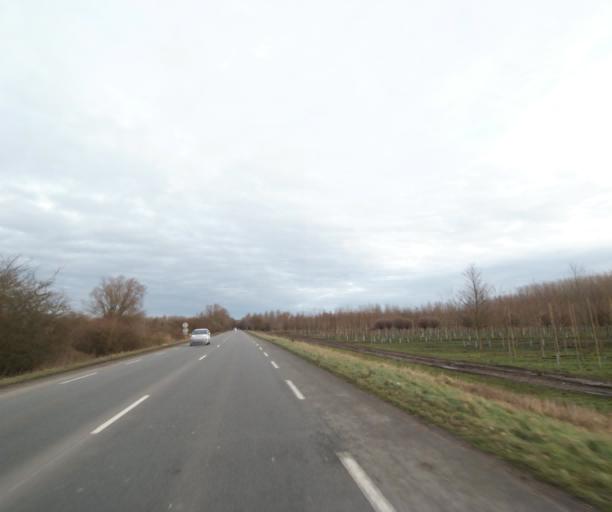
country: FR
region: Nord-Pas-de-Calais
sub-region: Departement du Nord
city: Vicq
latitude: 50.4278
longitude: 3.5993
